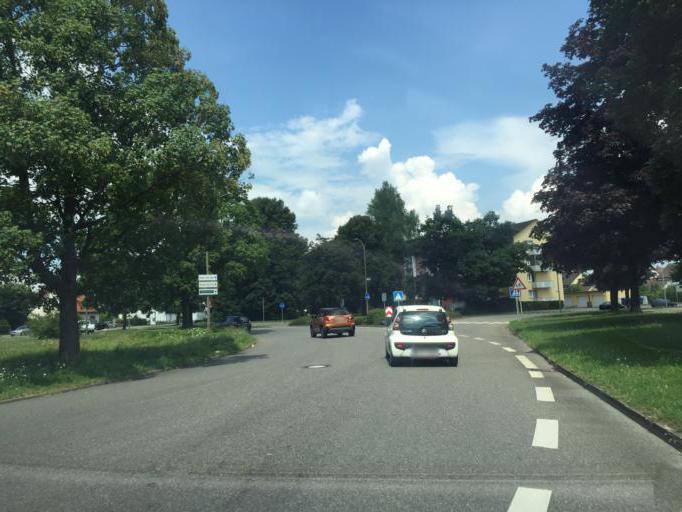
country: DE
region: Baden-Wuerttemberg
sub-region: Freiburg Region
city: Rielasingen-Worblingen
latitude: 47.7454
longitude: 8.8515
